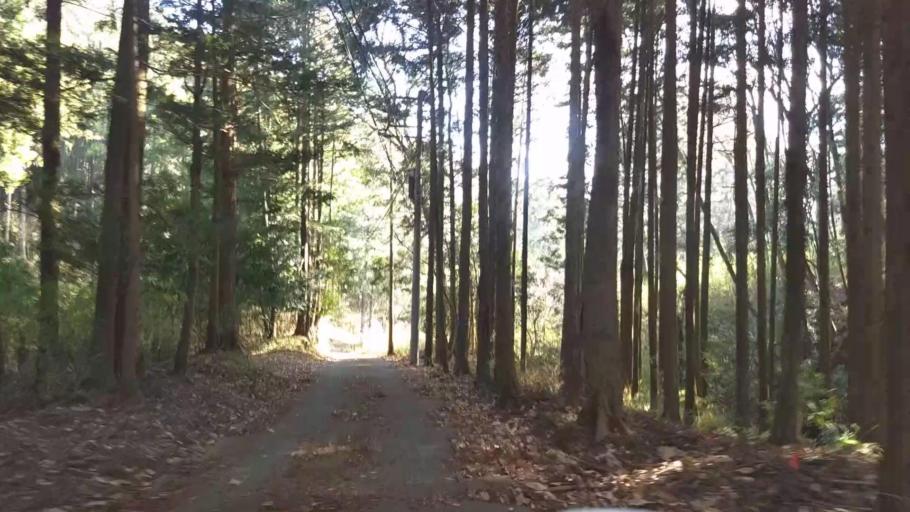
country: JP
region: Kanagawa
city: Isehara
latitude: 35.4437
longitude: 139.2862
